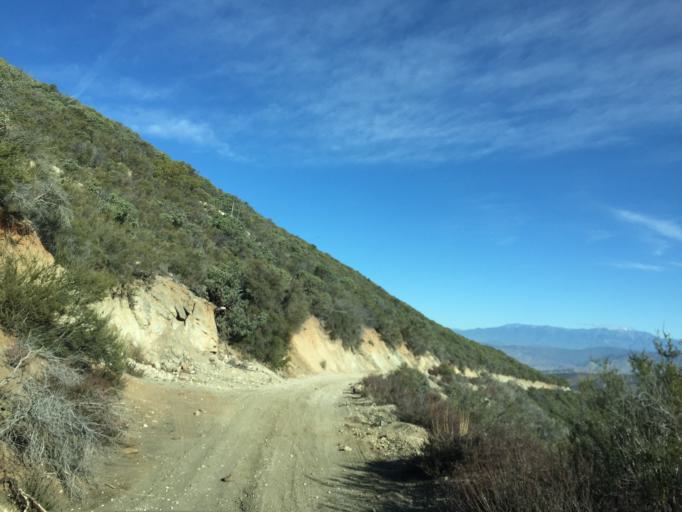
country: US
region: California
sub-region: Riverside County
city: Anza
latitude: 33.6176
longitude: -116.8109
